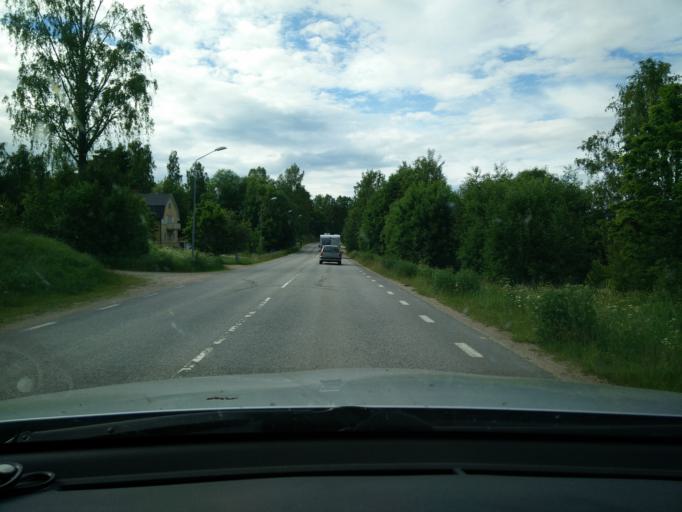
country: SE
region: Gaevleborg
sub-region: Nordanstigs Kommun
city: Bergsjoe
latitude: 61.9711
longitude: 17.0558
